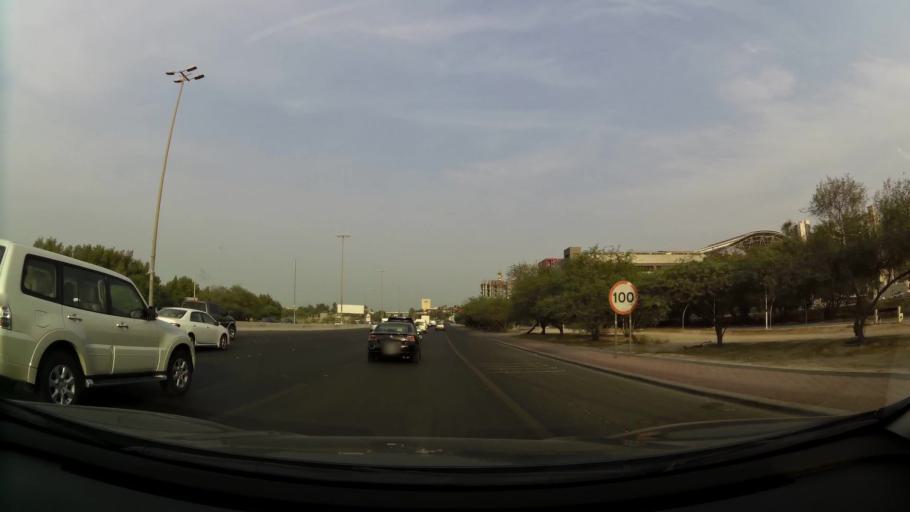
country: KW
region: Mubarak al Kabir
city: Sabah as Salim
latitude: 29.2671
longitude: 48.0790
